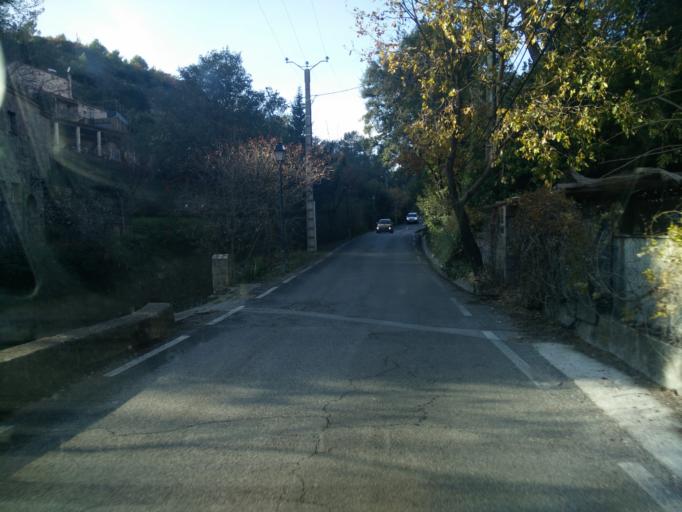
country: FR
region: Provence-Alpes-Cote d'Azur
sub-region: Departement du Var
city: Sollies-Toucas
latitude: 43.2028
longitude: 6.0186
